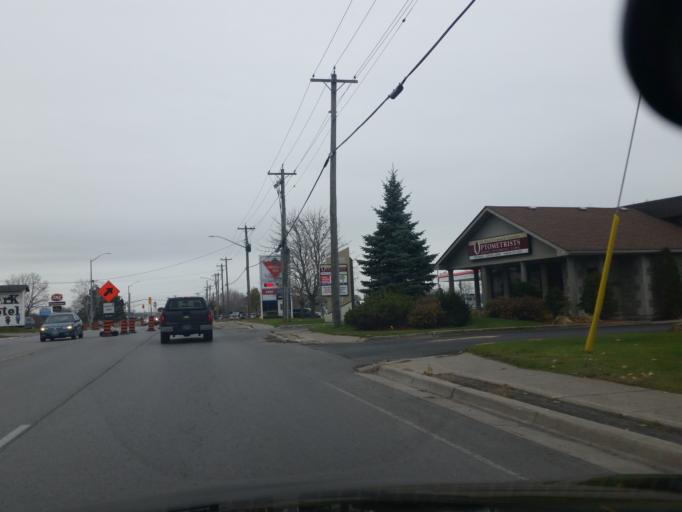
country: CA
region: Ontario
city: Quinte West
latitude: 44.1048
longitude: -77.5564
